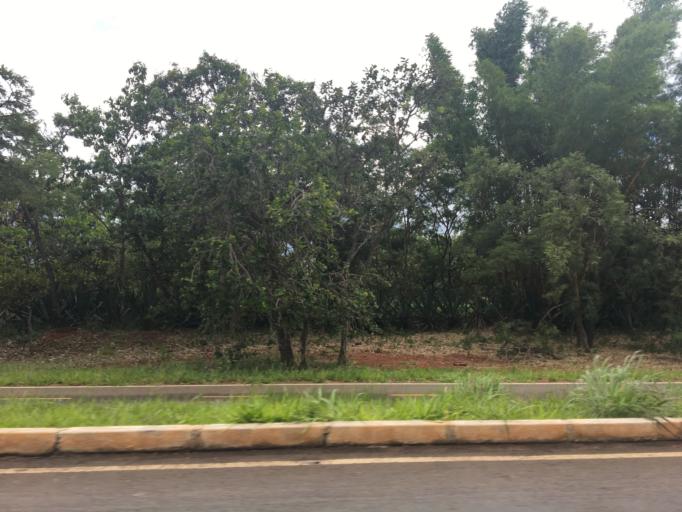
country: BR
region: Federal District
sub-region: Brasilia
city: Brasilia
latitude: -15.8985
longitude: -47.9295
